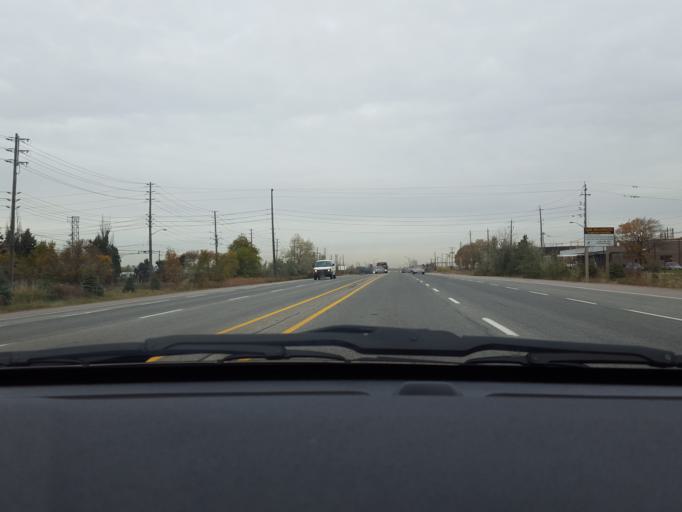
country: CA
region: Ontario
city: Etobicoke
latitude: 43.6929
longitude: -79.5842
